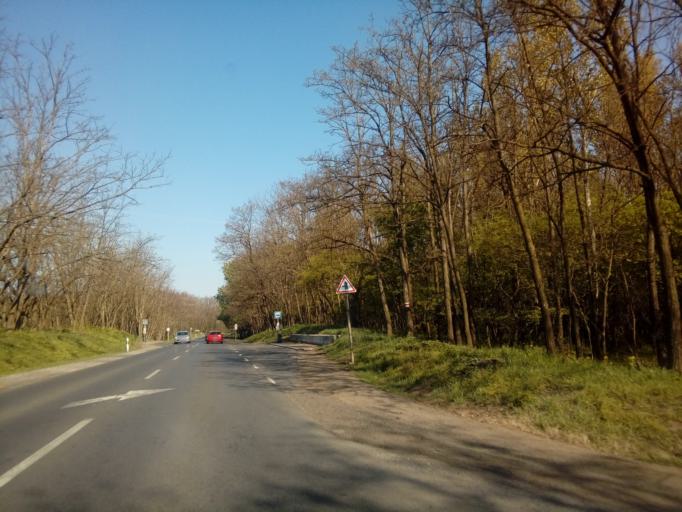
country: HU
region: Szabolcs-Szatmar-Bereg
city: Nyiregyhaza
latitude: 47.9131
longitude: 21.7758
